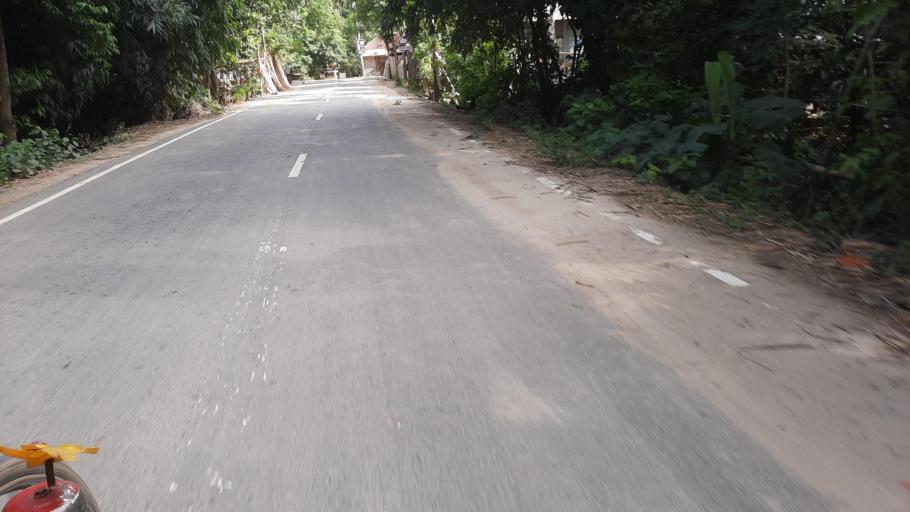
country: BD
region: Khulna
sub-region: Magura
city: Magura
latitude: 23.4487
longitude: 89.6148
